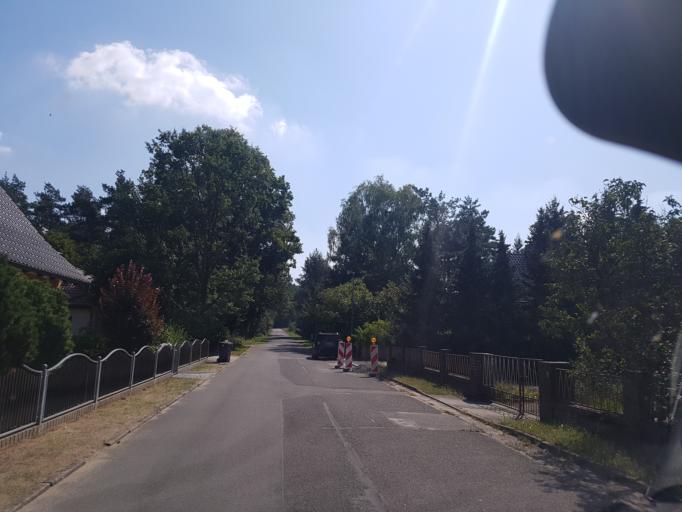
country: DE
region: Brandenburg
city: Elsterwerda
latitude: 51.4998
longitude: 13.4993
